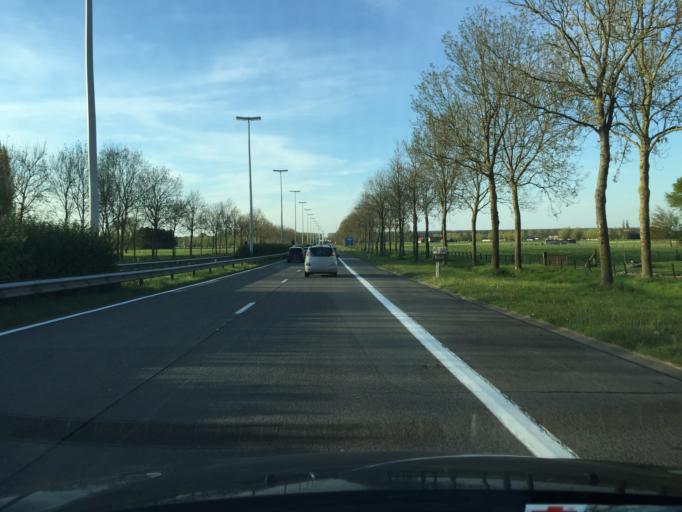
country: BE
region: Flanders
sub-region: Provincie Oost-Vlaanderen
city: Maldegem
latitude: 51.2088
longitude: 3.4628
